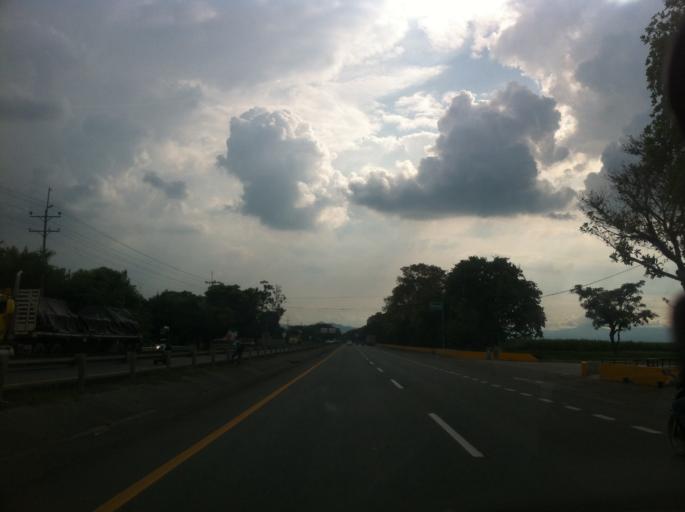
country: CO
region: Valle del Cauca
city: Tulua
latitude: 4.0492
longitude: -76.2049
